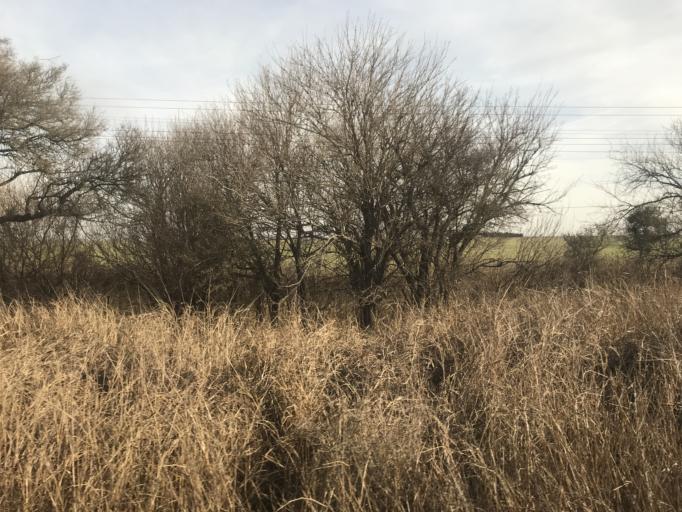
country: AR
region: Cordoba
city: Laguna Larga
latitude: -31.7585
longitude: -63.8192
